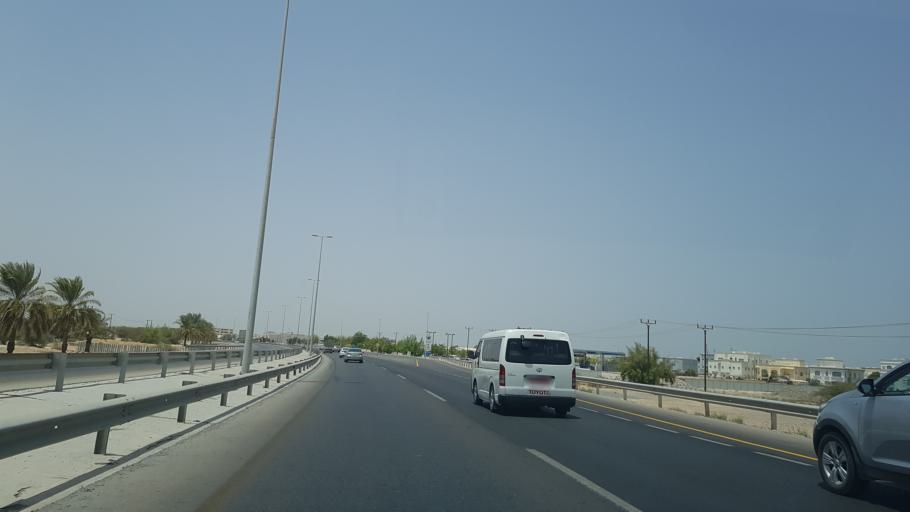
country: OM
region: Muhafazat Masqat
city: As Sib al Jadidah
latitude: 23.5888
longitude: 58.2452
